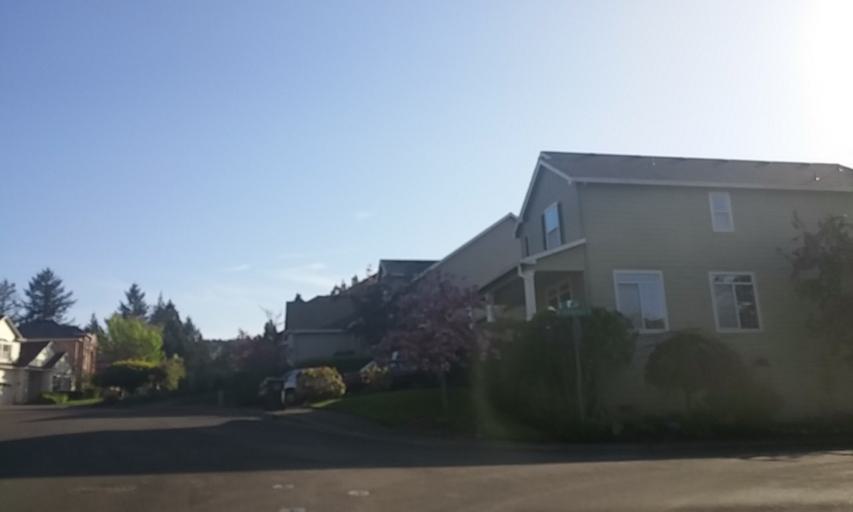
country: US
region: Oregon
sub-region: Washington County
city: Cedar Mill
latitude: 45.5465
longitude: -122.7955
